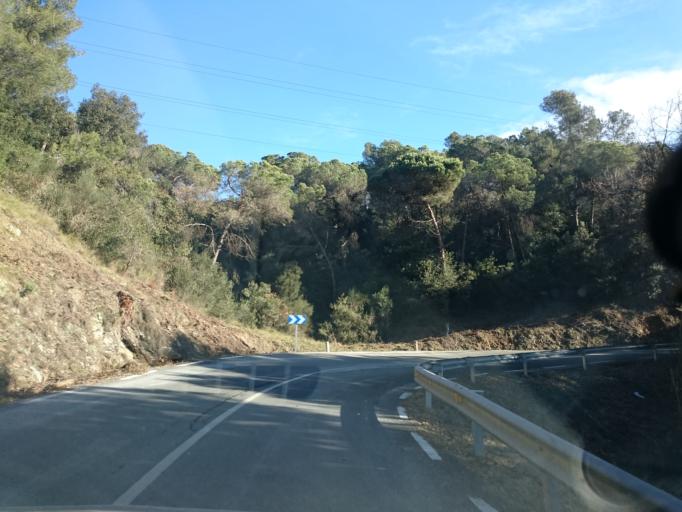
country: ES
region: Catalonia
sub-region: Provincia de Barcelona
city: Molins de Rei
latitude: 41.4287
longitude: 2.0443
